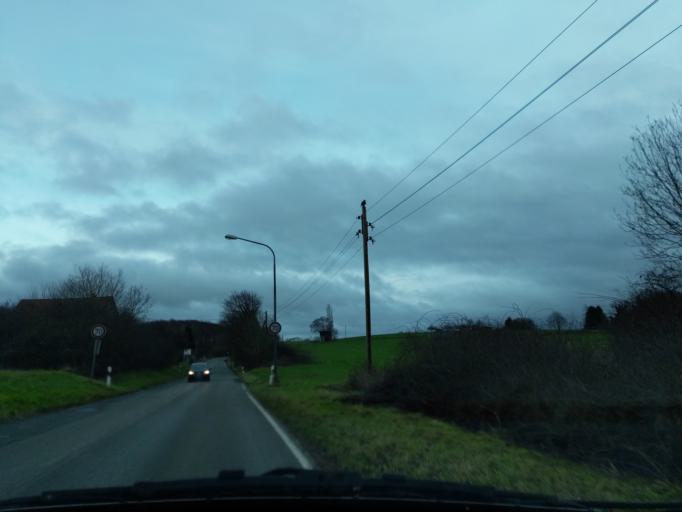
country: DE
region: North Rhine-Westphalia
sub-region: Regierungsbezirk Dusseldorf
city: Remscheid
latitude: 51.1390
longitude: 7.1610
